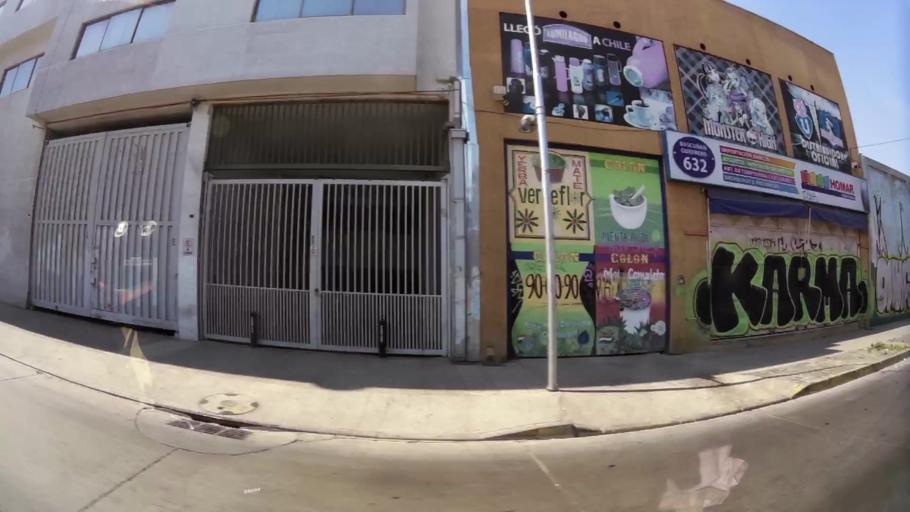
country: CL
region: Santiago Metropolitan
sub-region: Provincia de Santiago
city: Santiago
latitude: -33.4574
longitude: -70.6738
